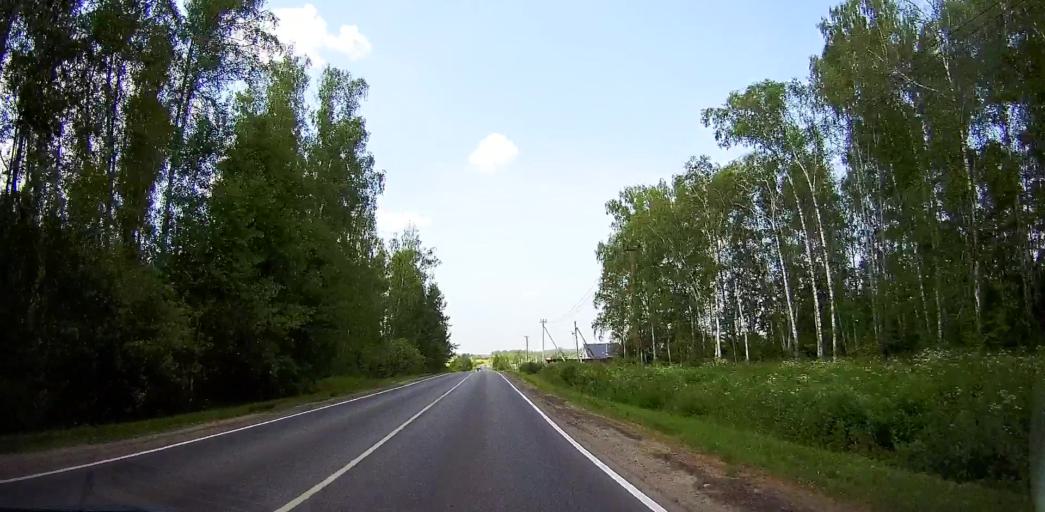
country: RU
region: Moskovskaya
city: Mikhnevo
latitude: 55.1708
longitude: 37.9628
